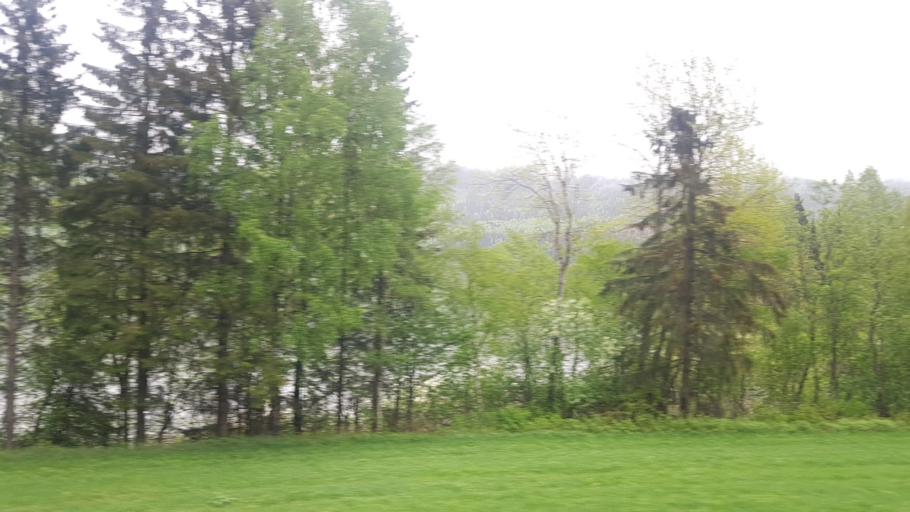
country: NO
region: Oppland
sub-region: Oyer
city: Tretten
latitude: 61.3361
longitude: 10.2854
